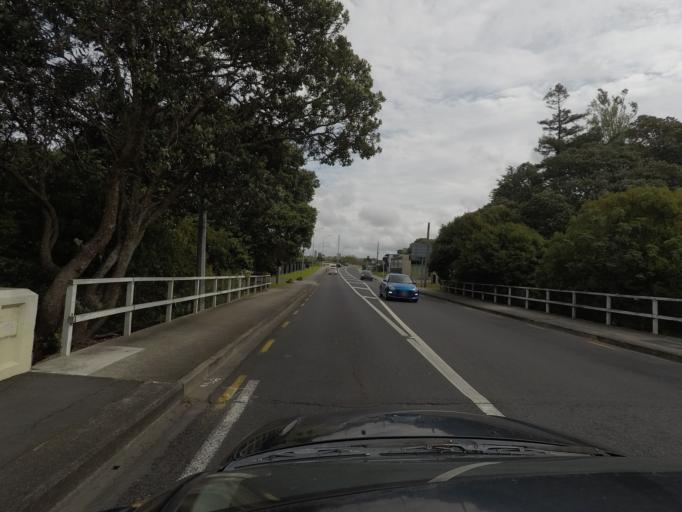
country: NZ
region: Auckland
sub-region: Auckland
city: Auckland
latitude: -36.8617
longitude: 174.8123
